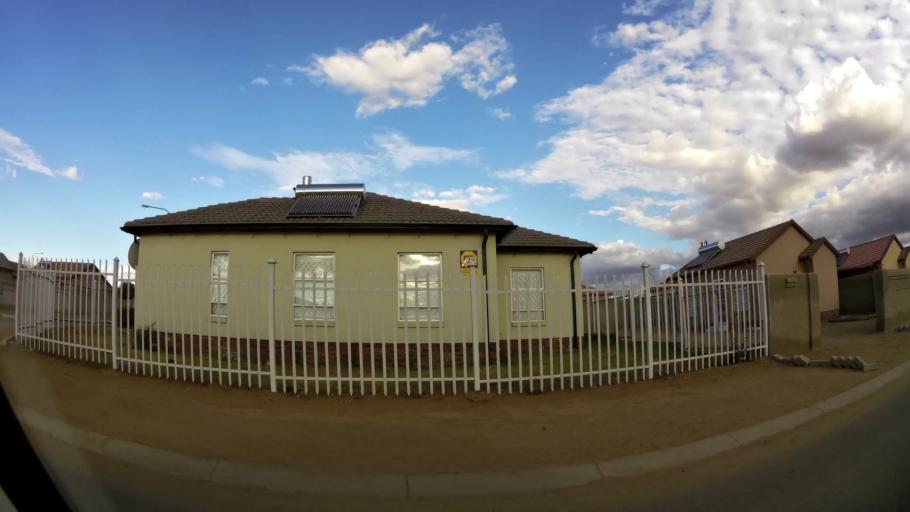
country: ZA
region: Limpopo
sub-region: Capricorn District Municipality
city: Polokwane
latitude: -23.9246
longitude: 29.4174
